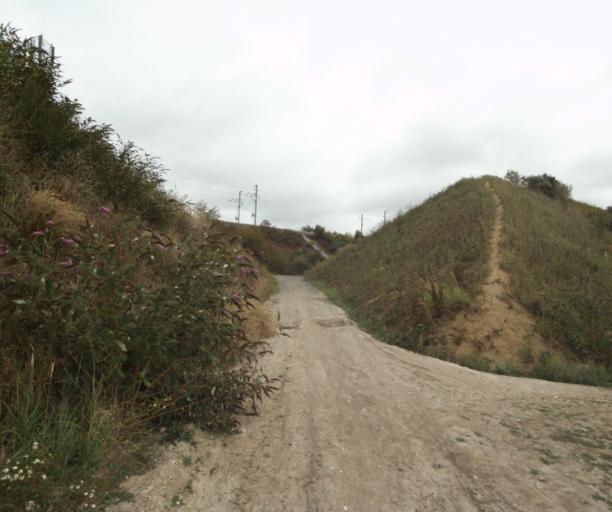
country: FR
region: Nord-Pas-de-Calais
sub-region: Departement du Nord
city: Lezennes
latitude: 50.5999
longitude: 3.1214
